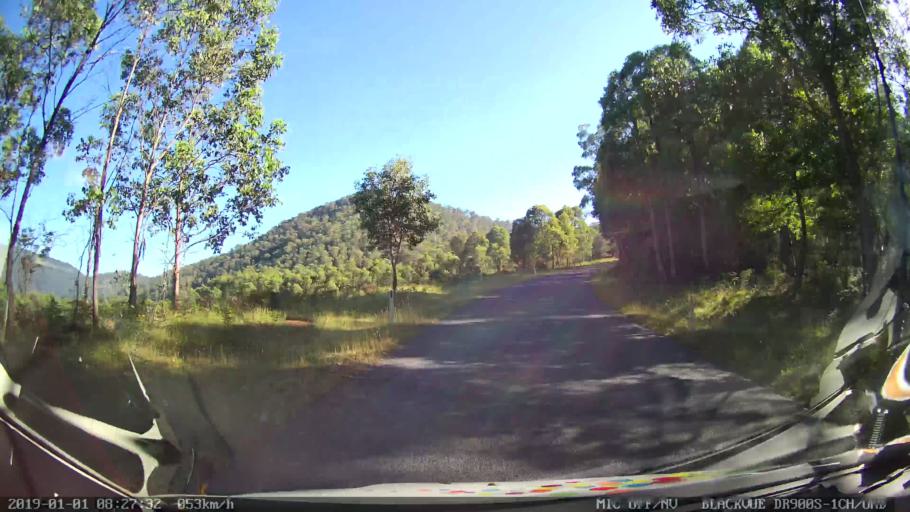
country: AU
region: New South Wales
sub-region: Snowy River
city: Jindabyne
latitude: -36.3809
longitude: 148.1841
